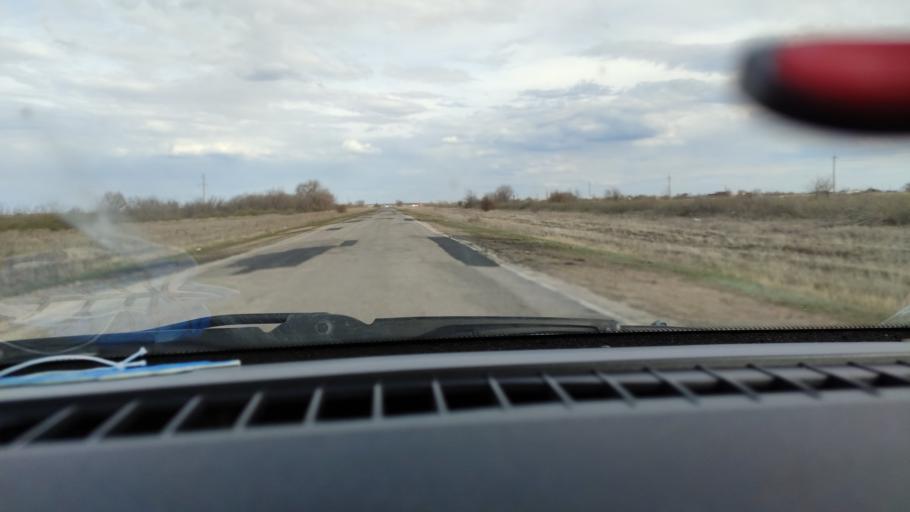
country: RU
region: Saratov
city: Rovnoye
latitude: 51.0644
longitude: 46.0118
